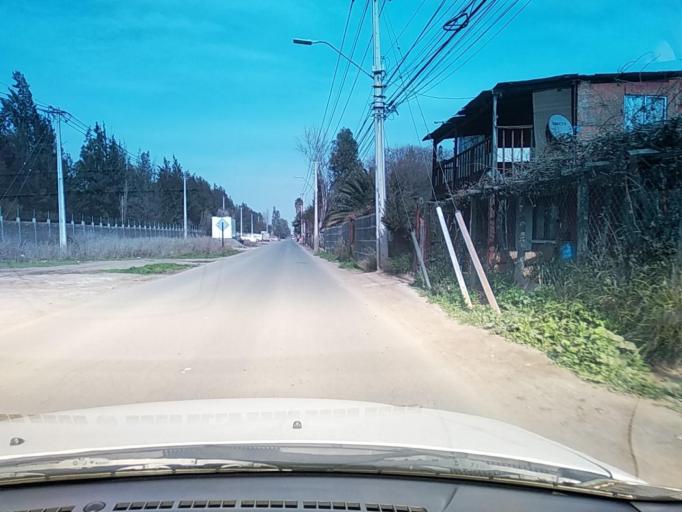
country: CL
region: Santiago Metropolitan
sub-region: Provincia de Chacabuco
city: Chicureo Abajo
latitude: -33.2887
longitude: -70.7277
